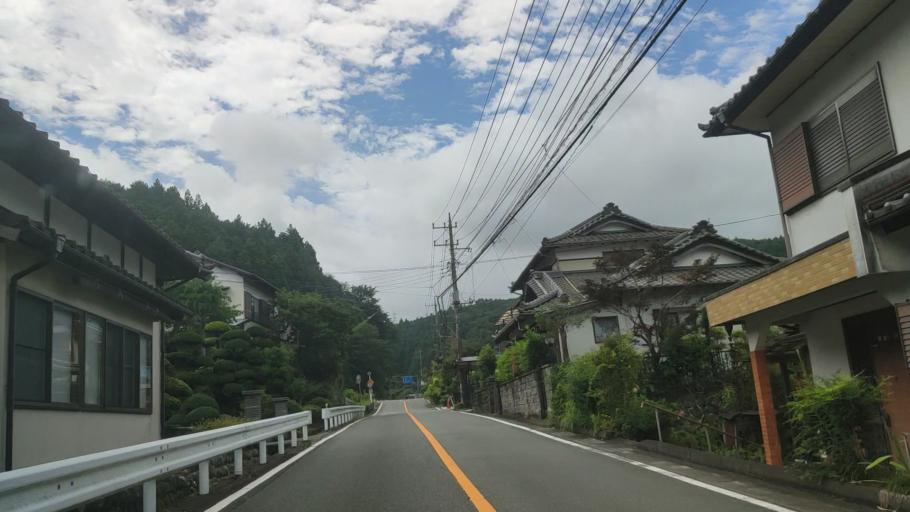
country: JP
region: Shizuoka
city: Fujinomiya
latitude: 35.2177
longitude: 138.5180
